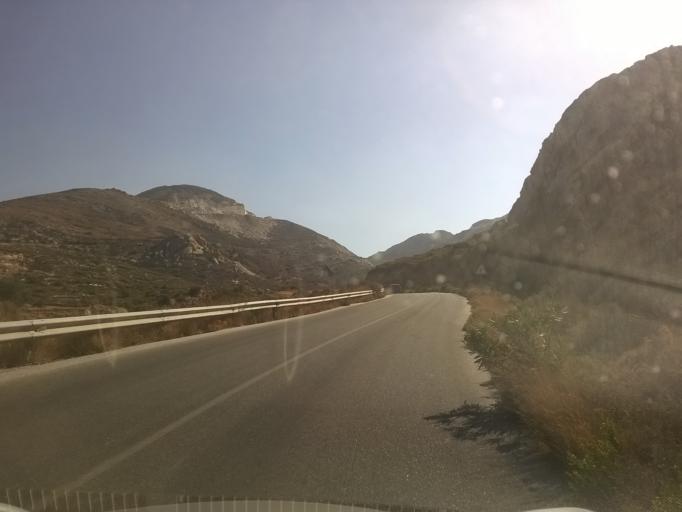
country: GR
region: South Aegean
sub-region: Nomos Kykladon
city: Filotion
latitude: 37.0919
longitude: 25.4586
